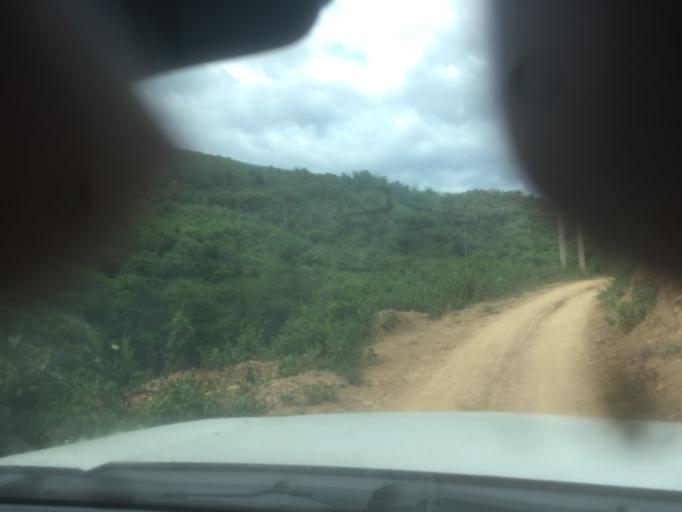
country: LA
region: Phongsali
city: Khoa
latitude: 20.9098
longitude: 102.5598
